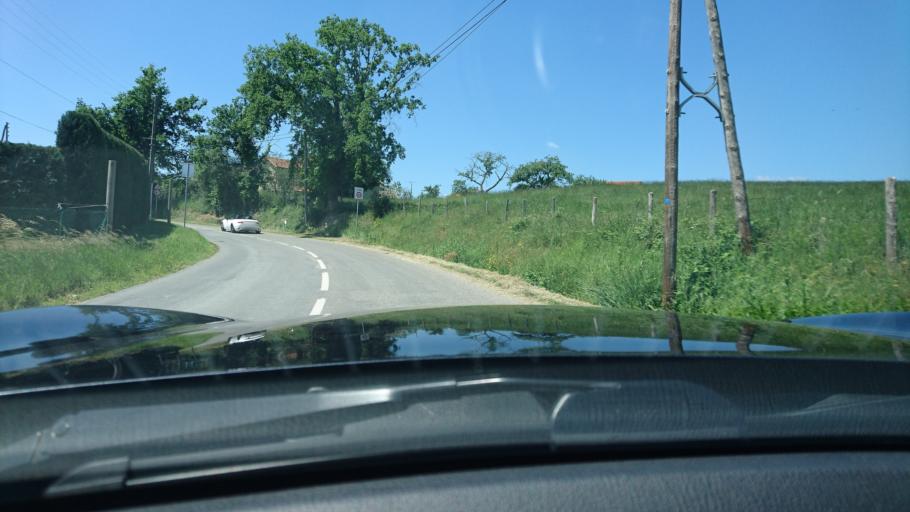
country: FR
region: Rhone-Alpes
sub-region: Departement de la Loire
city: Rozier-en-Donzy
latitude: 45.7937
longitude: 4.3024
